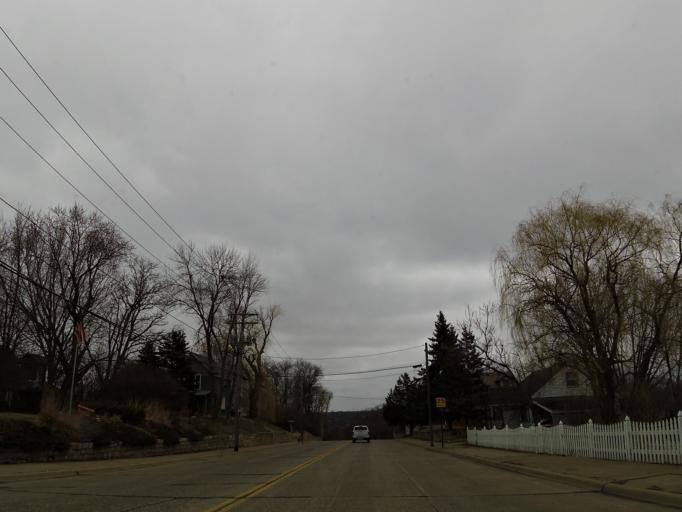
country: US
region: Minnesota
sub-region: Washington County
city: Stillwater
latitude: 45.0548
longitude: -92.8166
